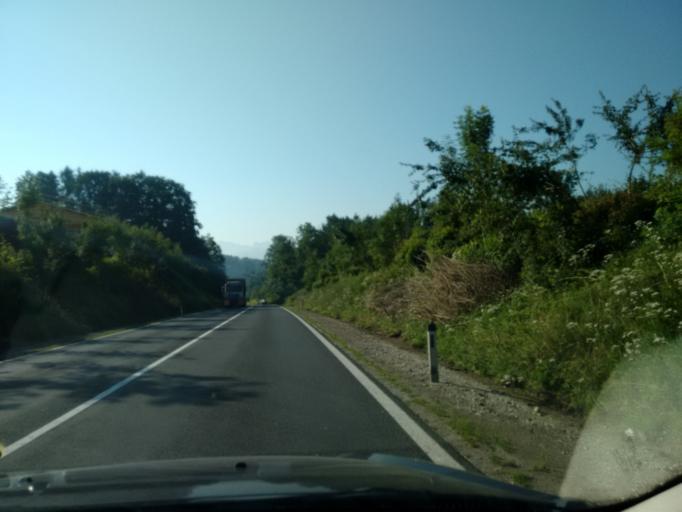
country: AT
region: Upper Austria
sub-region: Politischer Bezirk Gmunden
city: Altmunster
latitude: 47.9531
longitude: 13.7453
